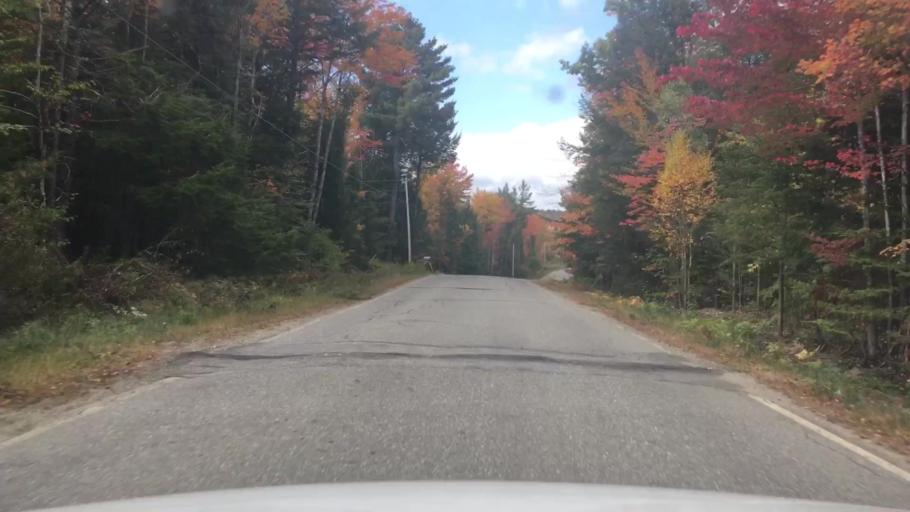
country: US
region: Maine
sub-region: Knox County
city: Washington
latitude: 44.3297
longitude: -69.3686
